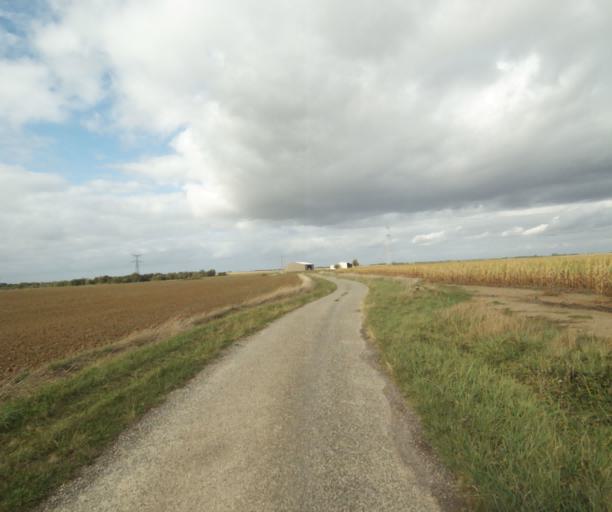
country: FR
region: Midi-Pyrenees
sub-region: Departement du Tarn-et-Garonne
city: Beaumont-de-Lomagne
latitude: 43.9028
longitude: 1.1035
